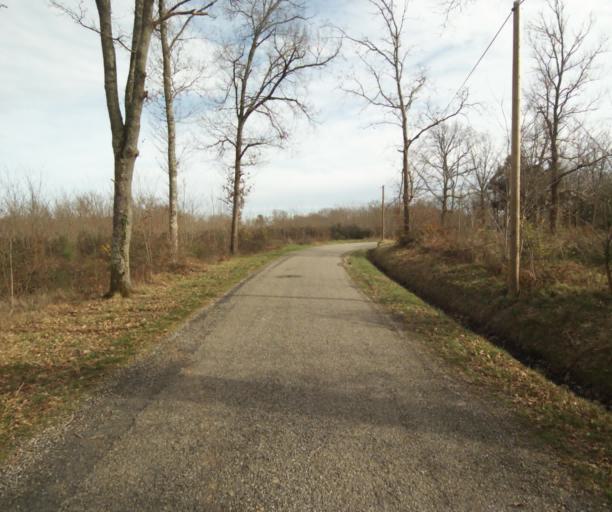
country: FR
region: Aquitaine
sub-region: Departement des Landes
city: Gabarret
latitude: 43.9767
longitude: 0.0299
